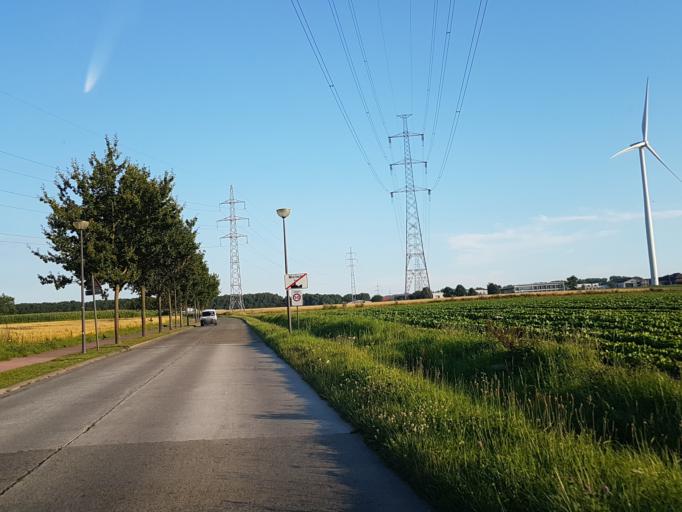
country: BE
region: Flanders
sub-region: Provincie Vlaams-Brabant
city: Merchtem
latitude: 50.9234
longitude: 4.2339
